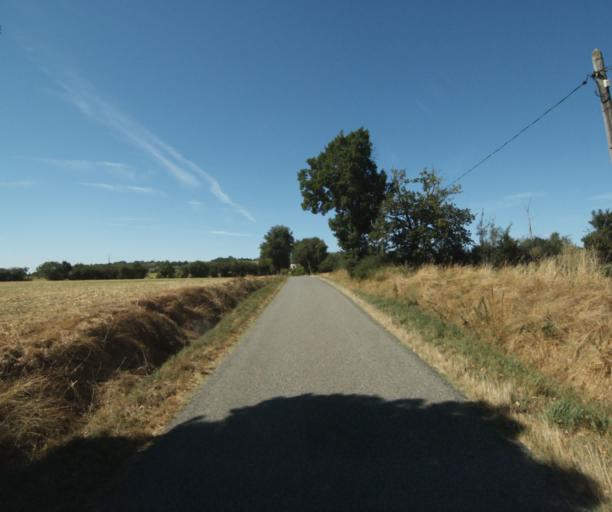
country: FR
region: Midi-Pyrenees
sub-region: Departement de la Haute-Garonne
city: Auriac-sur-Vendinelle
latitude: 43.5150
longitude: 1.8885
